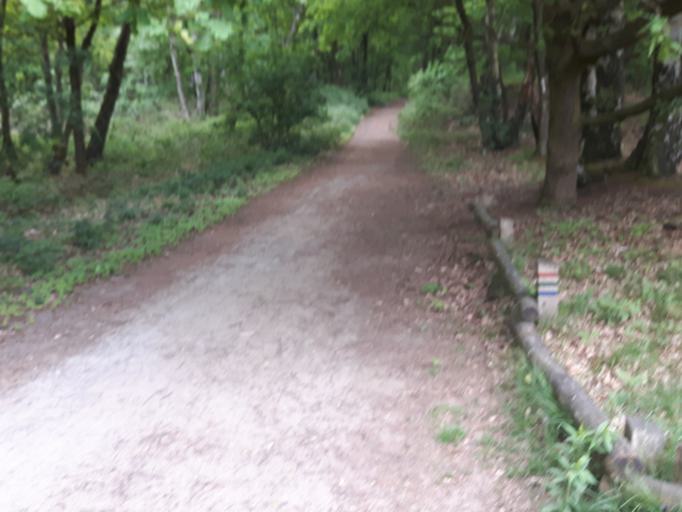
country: DE
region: North Rhine-Westphalia
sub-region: Regierungsbezirk Munster
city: Haltern
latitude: 51.7385
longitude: 7.2286
